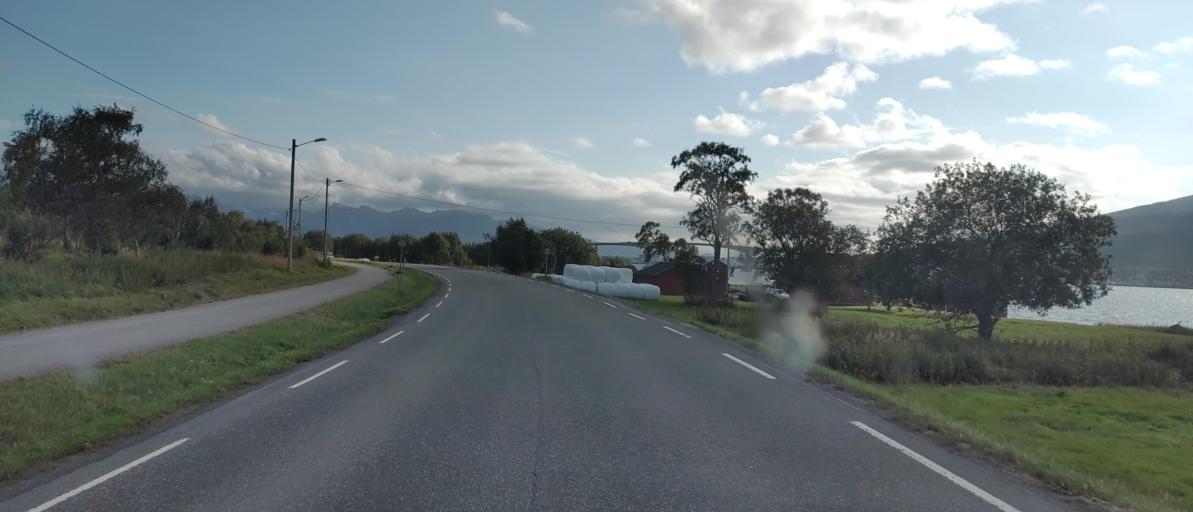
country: NO
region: Nordland
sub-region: Sortland
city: Sortland
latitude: 68.7162
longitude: 15.4407
